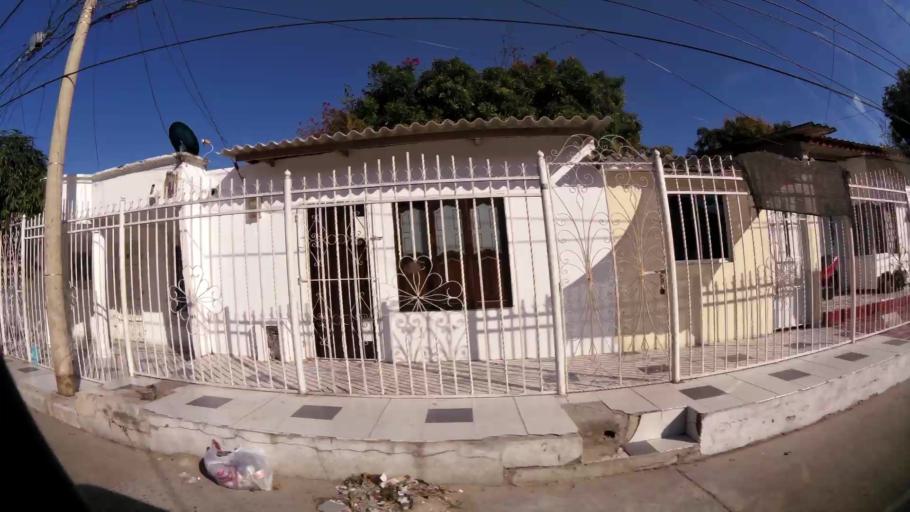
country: CO
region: Atlantico
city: Barranquilla
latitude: 10.9663
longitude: -74.7842
